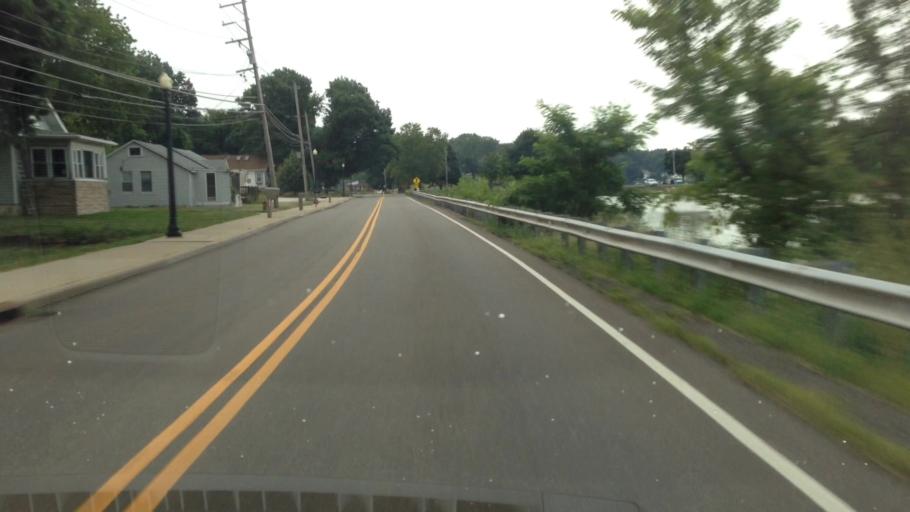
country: US
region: Ohio
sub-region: Summit County
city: Portage Lakes
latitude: 41.0053
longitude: -81.5487
